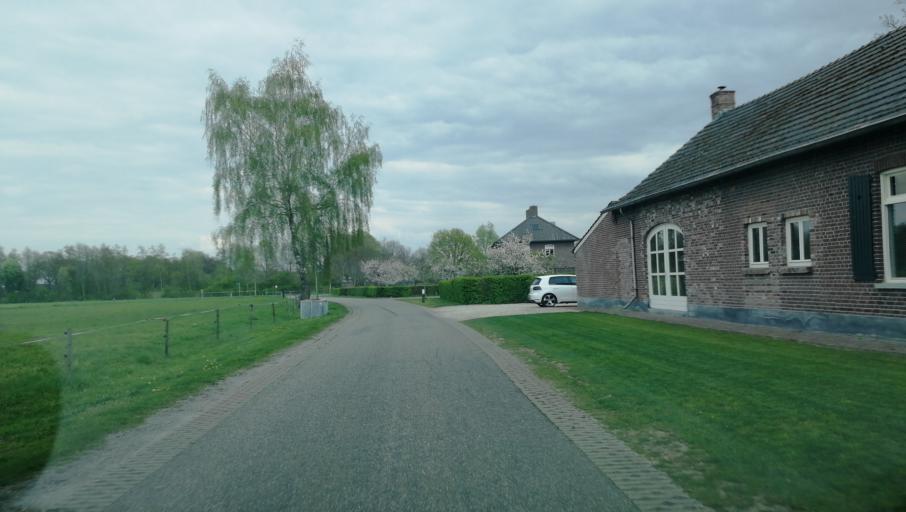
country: NL
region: Limburg
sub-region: Gemeente Peel en Maas
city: Maasbree
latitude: 51.3981
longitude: 6.0465
